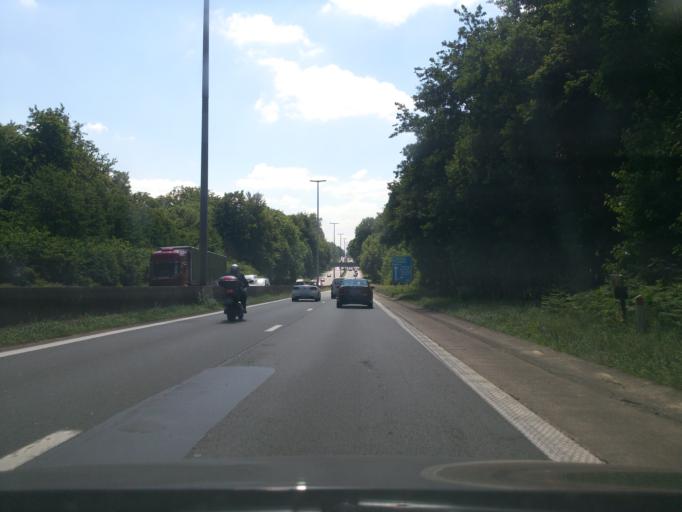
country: BE
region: Flanders
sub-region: Provincie Vlaams-Brabant
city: Hoeilaart
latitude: 50.7749
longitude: 4.4477
